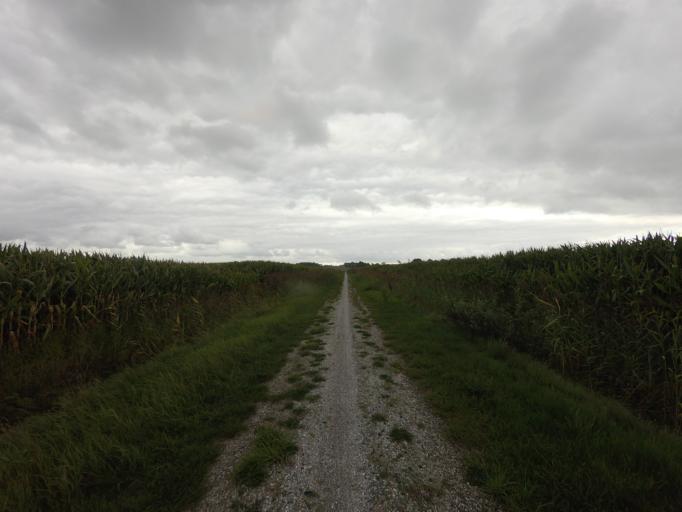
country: NL
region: Friesland
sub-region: Gemeente Weststellingwerf
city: Noordwolde
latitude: 52.9405
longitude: 6.1875
